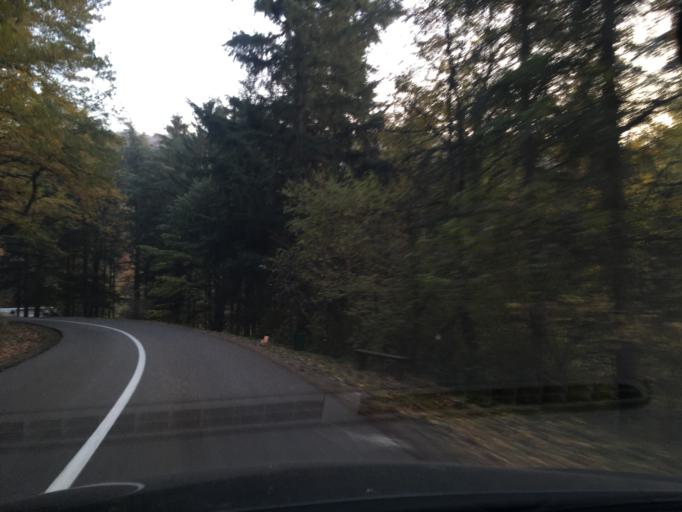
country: RS
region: Central Serbia
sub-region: Belgrade
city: Sopot
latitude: 44.4730
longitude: 20.5722
